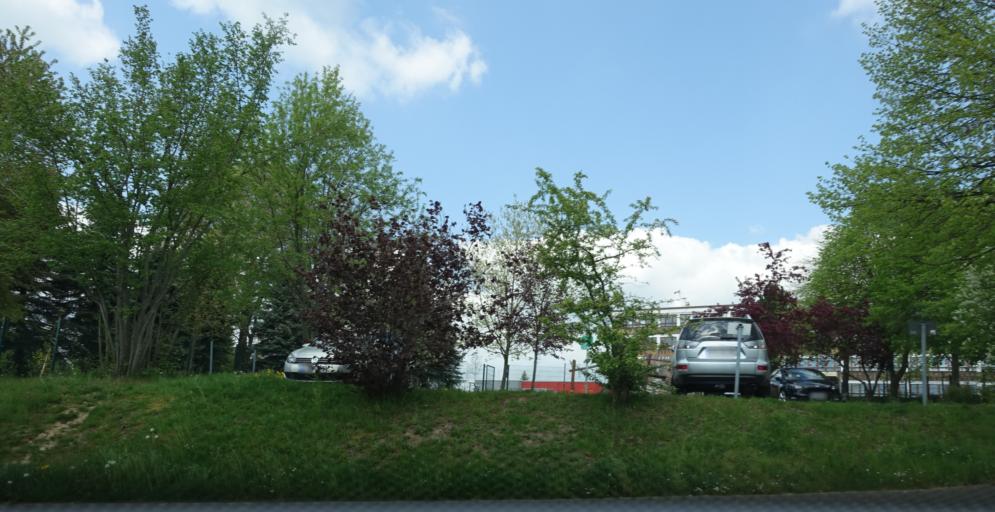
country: DE
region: Saxony
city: Eppendorf
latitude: 50.7996
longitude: 13.2307
